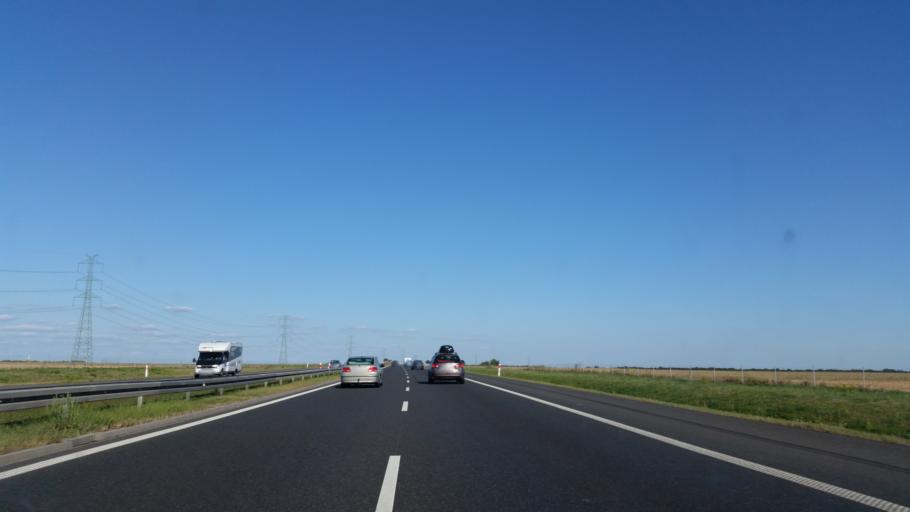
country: PL
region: Opole Voivodeship
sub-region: Powiat brzeski
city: Olszanka
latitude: 50.7369
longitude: 17.4793
